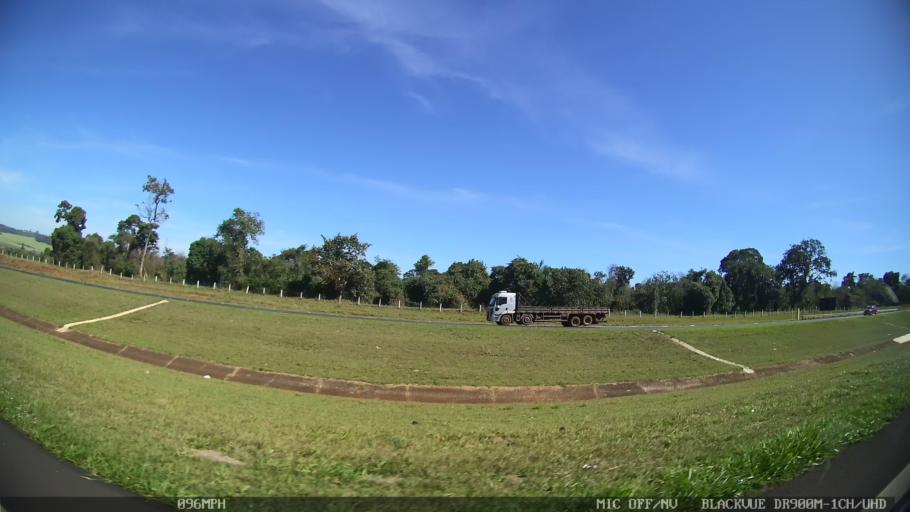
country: BR
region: Sao Paulo
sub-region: Santa Rita Do Passa Quatro
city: Santa Rita do Passa Quatro
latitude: -21.7260
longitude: -47.5866
